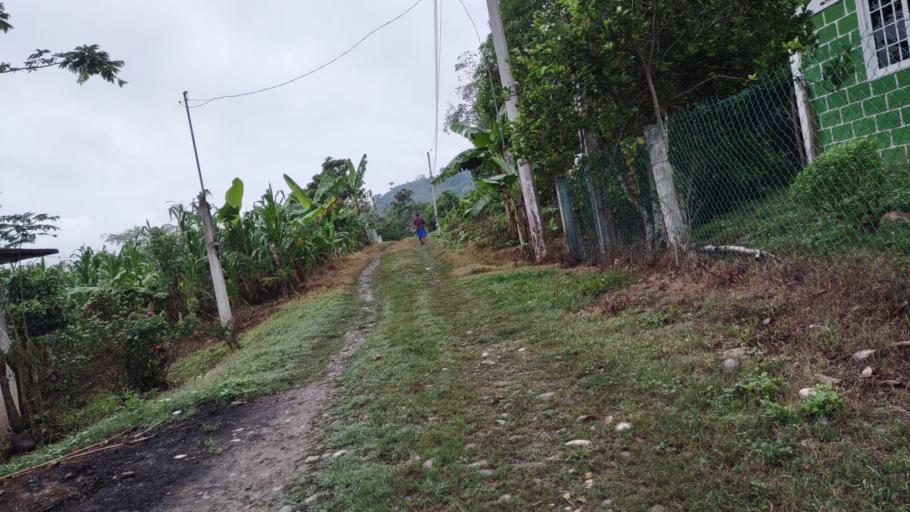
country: MX
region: Puebla
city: Espinal
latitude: 20.2637
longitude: -97.3677
